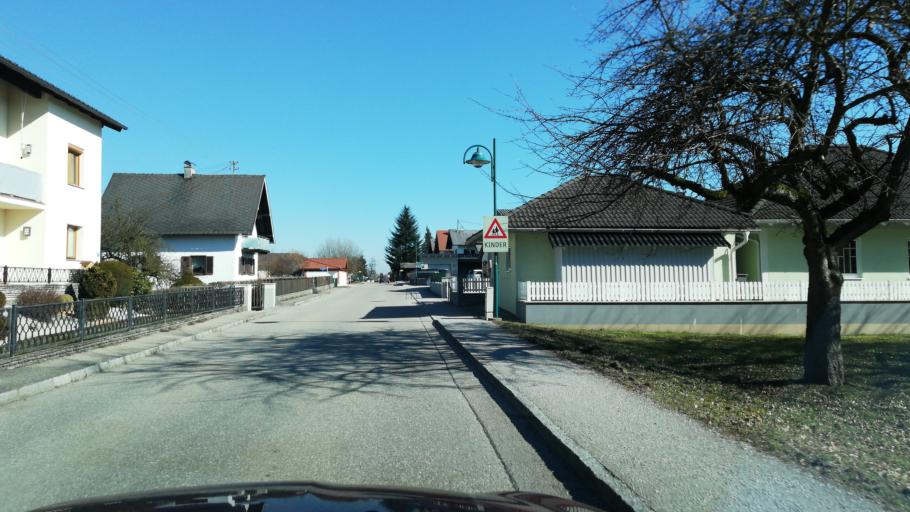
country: AT
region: Upper Austria
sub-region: Politischer Bezirk Vocklabruck
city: Redlham
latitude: 48.0269
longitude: 13.7303
